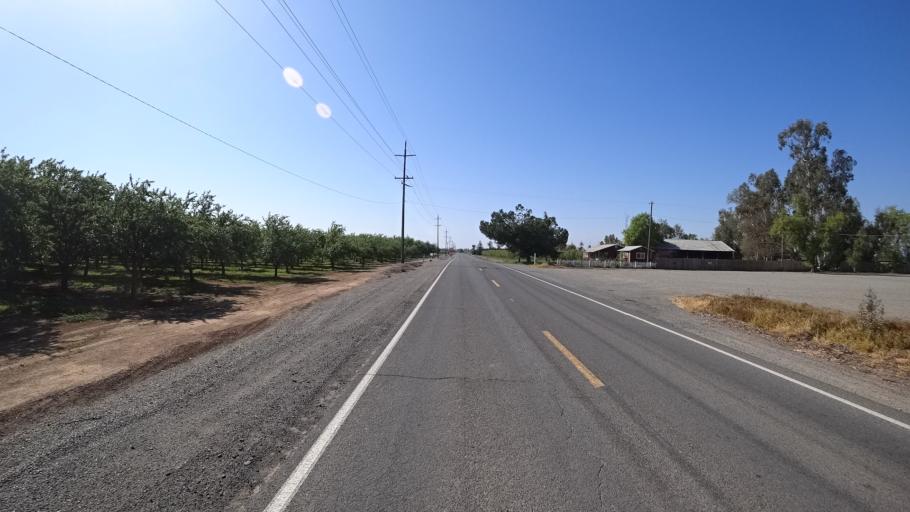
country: US
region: California
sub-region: Glenn County
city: Hamilton City
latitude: 39.6428
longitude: -122.0075
